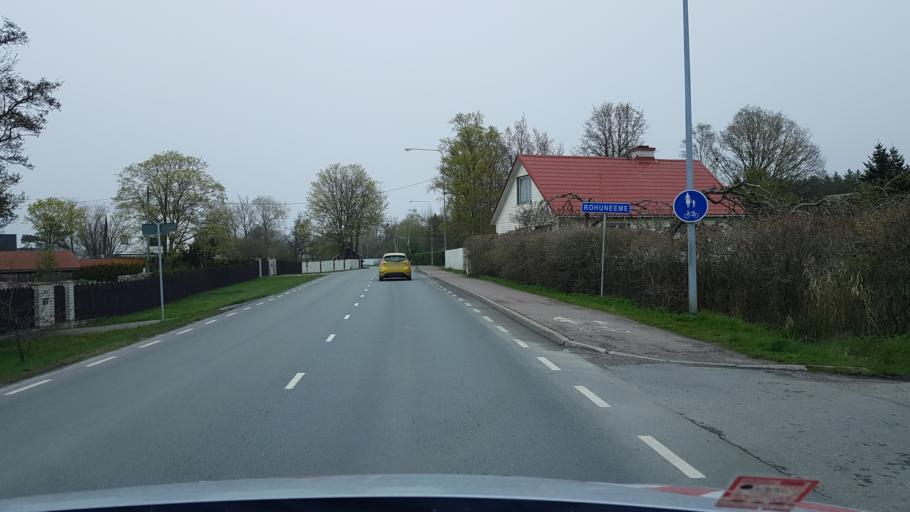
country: EE
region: Harju
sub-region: Viimsi vald
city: Rummu
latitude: 59.5570
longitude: 24.7961
